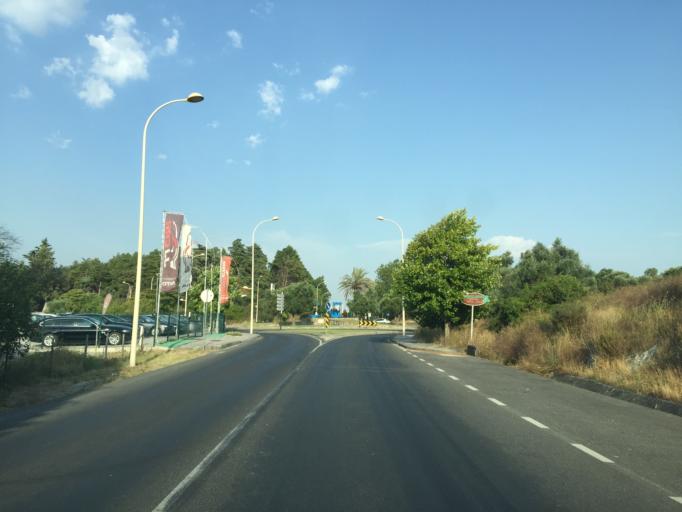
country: PT
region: Santarem
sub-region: Torres Novas
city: Torres Novas
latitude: 39.4755
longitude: -8.5609
